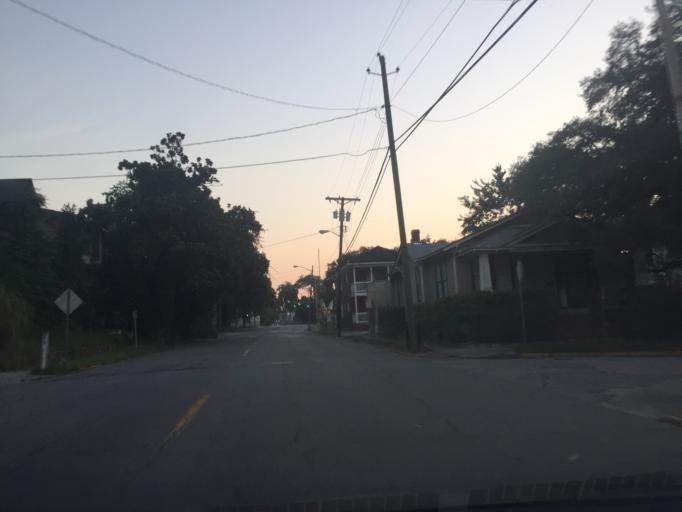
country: US
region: Georgia
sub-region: Chatham County
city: Savannah
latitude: 32.0547
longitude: -81.0962
